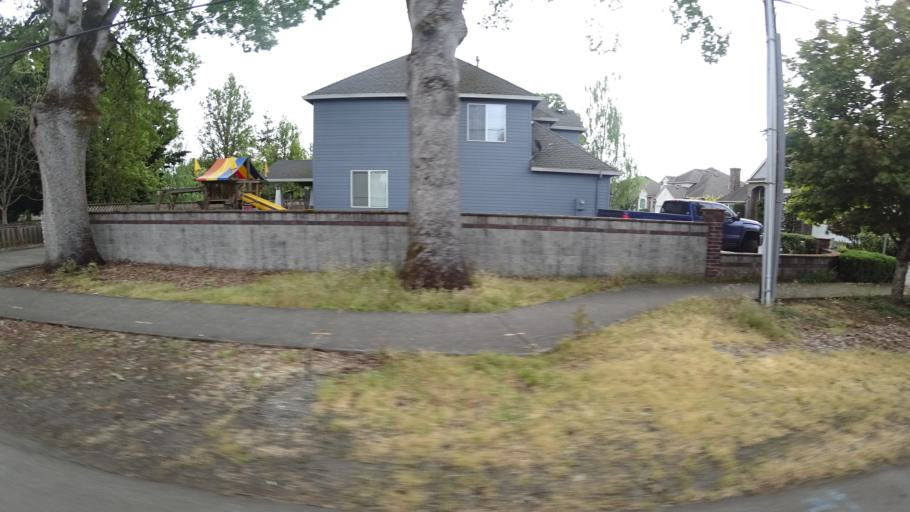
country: US
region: Oregon
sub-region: Washington County
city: Hillsboro
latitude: 45.5420
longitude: -122.9794
